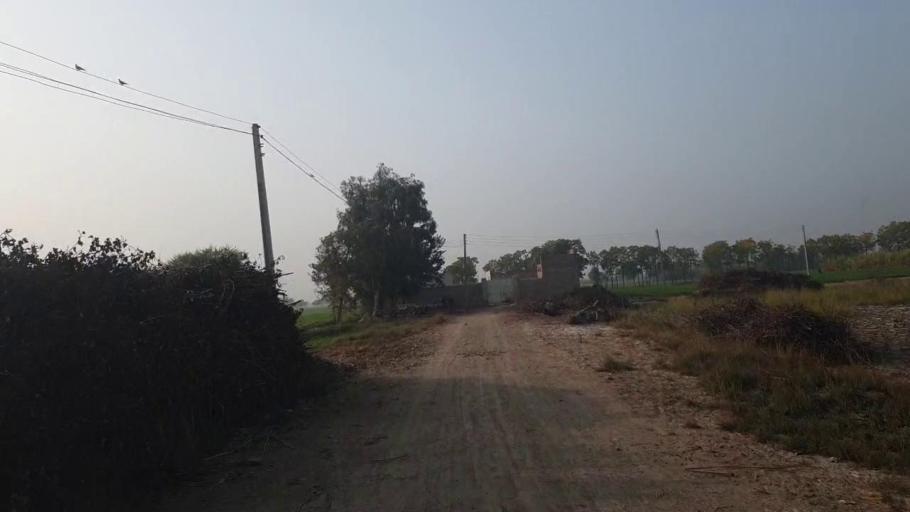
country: PK
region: Sindh
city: Shahdadpur
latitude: 25.8524
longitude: 68.5888
